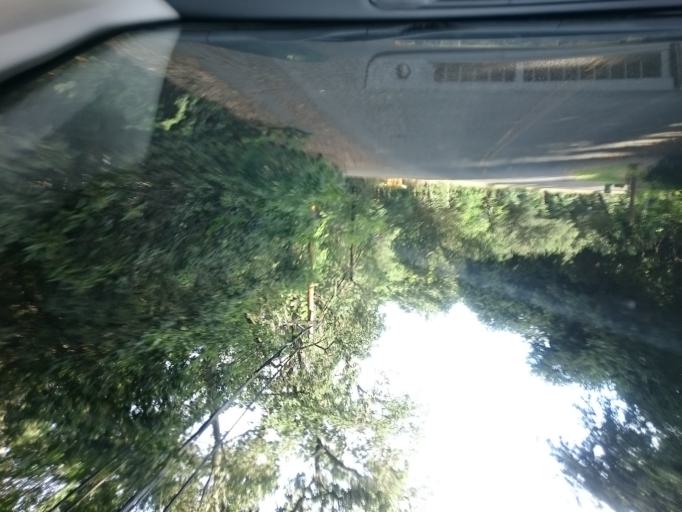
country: US
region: California
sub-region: Napa County
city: Saint Helena
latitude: 38.5180
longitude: -122.4718
